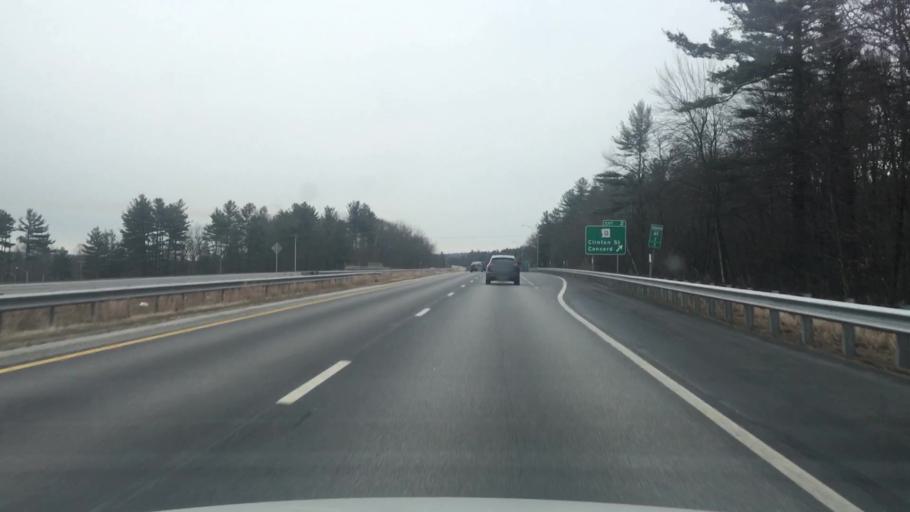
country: US
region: New Hampshire
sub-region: Merrimack County
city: Concord
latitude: 43.1809
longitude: -71.5691
